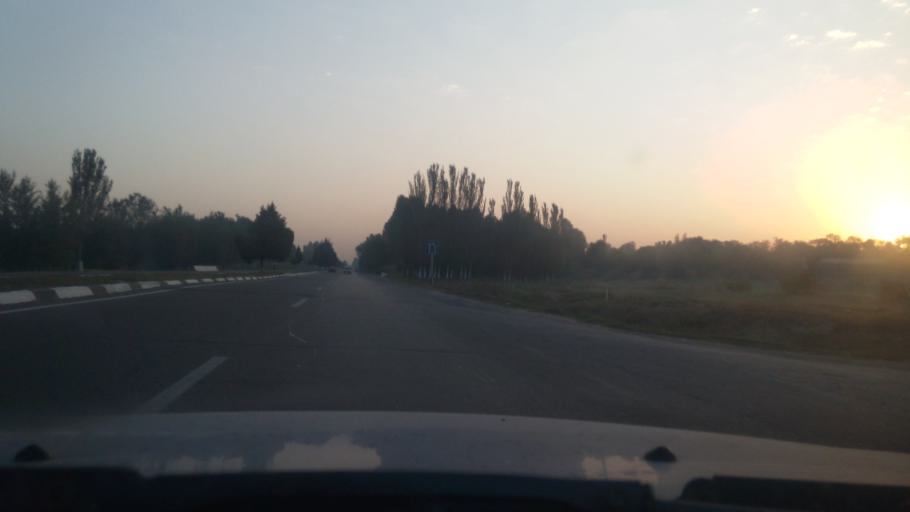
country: UZ
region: Toshkent
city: Amir Timur
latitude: 41.0671
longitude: 68.9192
